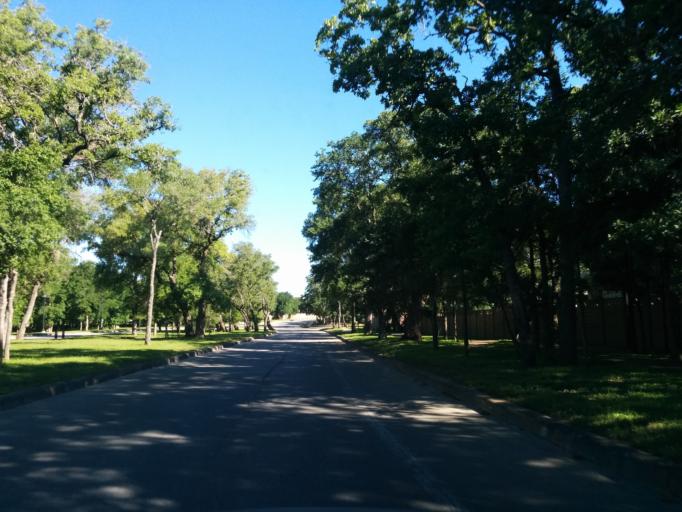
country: US
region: Texas
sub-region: Bexar County
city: Cross Mountain
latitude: 29.6690
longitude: -98.6405
